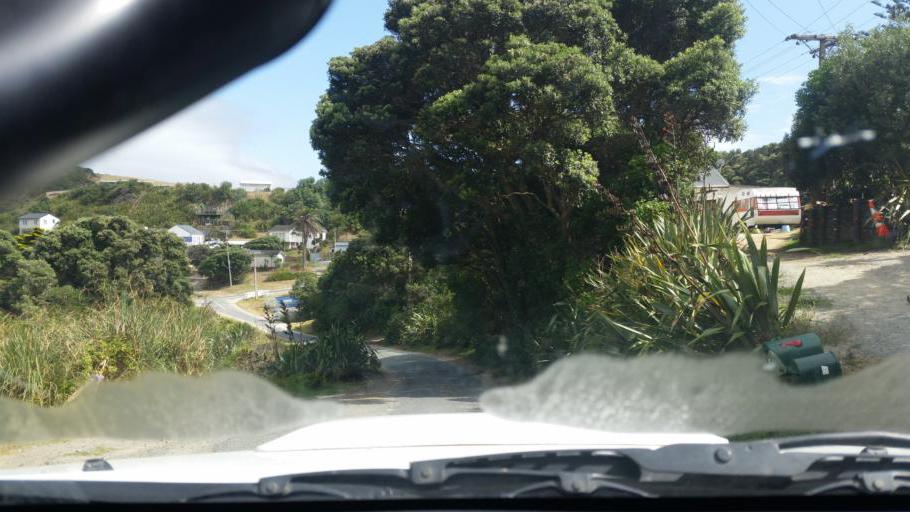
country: NZ
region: Northland
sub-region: Kaipara District
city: Dargaville
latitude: -35.9504
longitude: 173.7449
